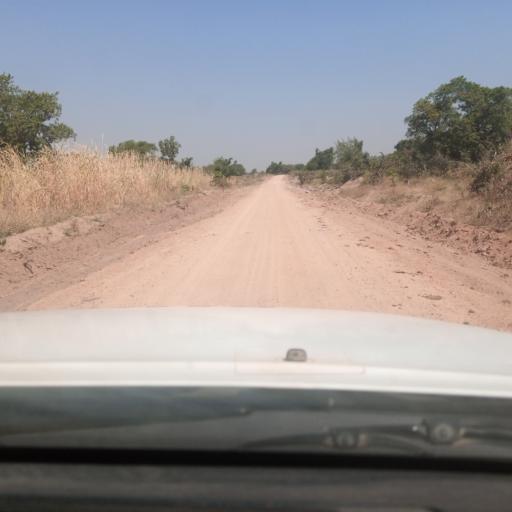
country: NG
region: Adamawa
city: Yola
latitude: 9.0510
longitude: 12.3874
